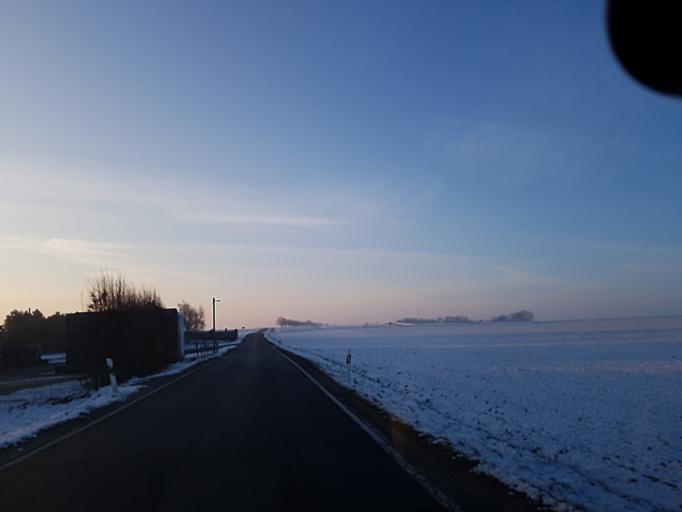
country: DE
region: Saxony
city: Mugeln
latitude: 51.2050
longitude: 13.0305
